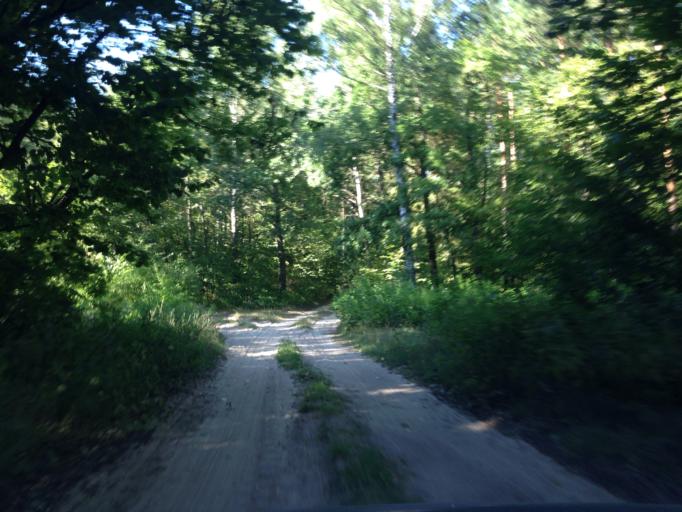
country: PL
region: Kujawsko-Pomorskie
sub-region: Powiat brodnicki
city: Gorzno
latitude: 53.1584
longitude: 19.6705
